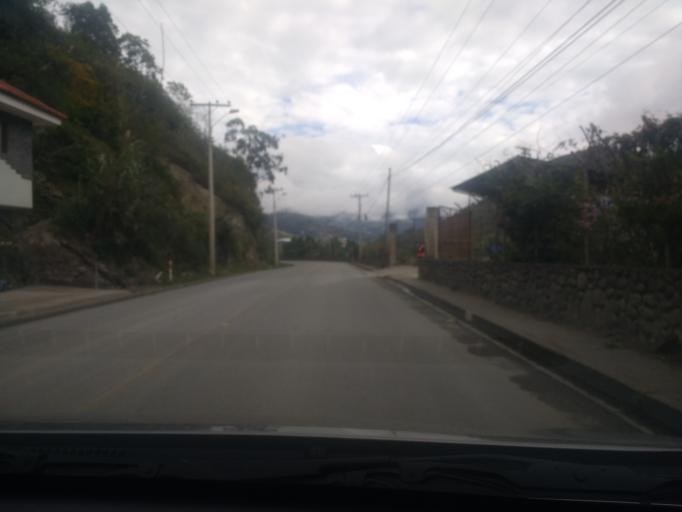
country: EC
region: Azuay
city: La Union
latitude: -2.8265
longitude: -78.7714
